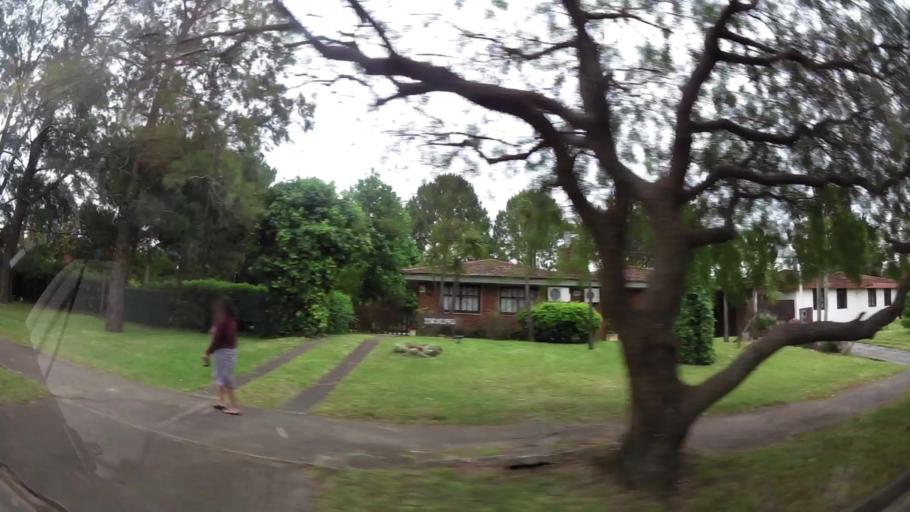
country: UY
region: Maldonado
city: Maldonado
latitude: -34.9119
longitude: -54.9720
